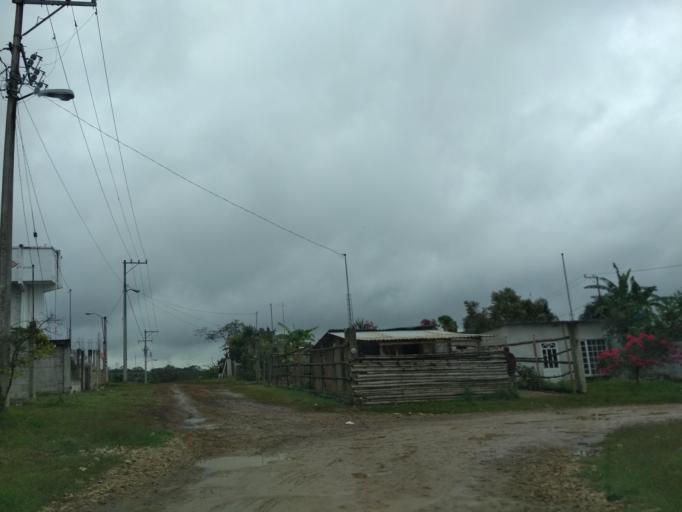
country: MX
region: Veracruz
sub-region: Cordoba
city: San Jose de Tapia
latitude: 18.8517
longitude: -96.9679
